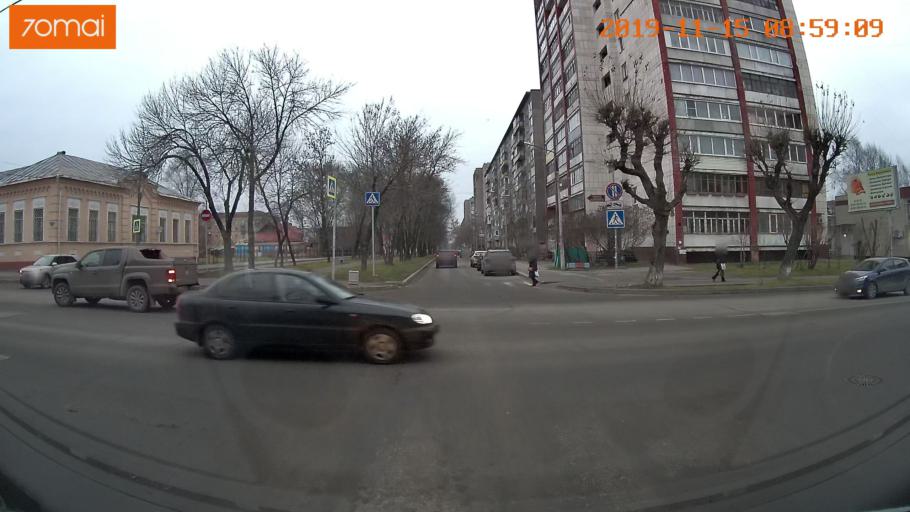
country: RU
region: Vologda
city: Cherepovets
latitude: 59.1284
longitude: 37.9241
